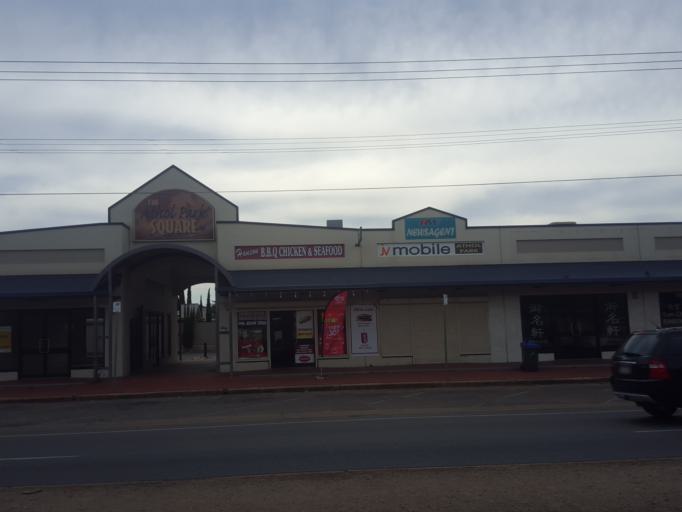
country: AU
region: South Australia
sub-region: Charles Sturt
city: Woodville North
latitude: -34.8558
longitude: 138.5471
